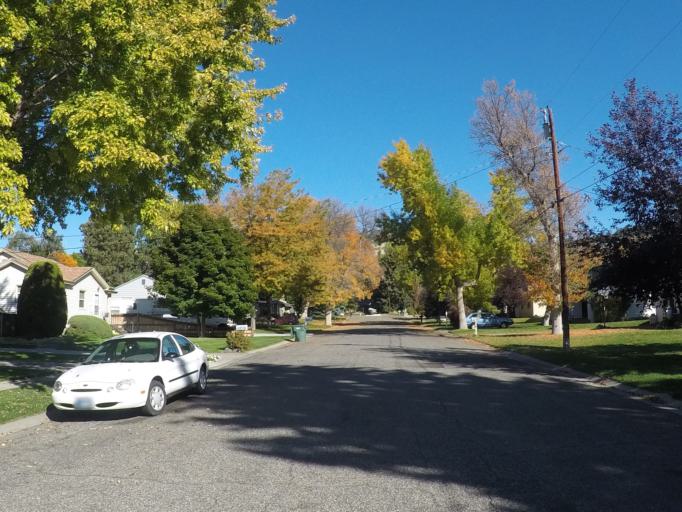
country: US
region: Montana
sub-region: Yellowstone County
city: Billings
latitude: 45.7968
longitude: -108.5847
